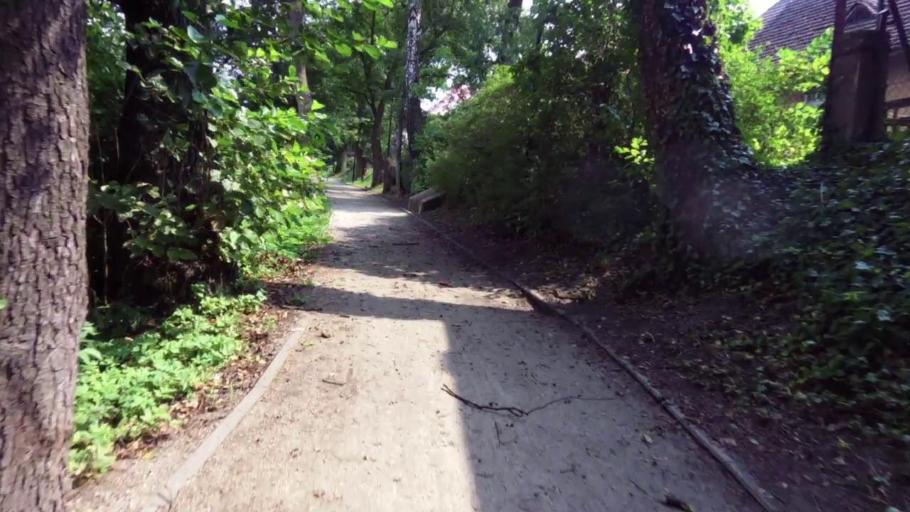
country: PL
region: West Pomeranian Voivodeship
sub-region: Powiat choszczenski
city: Choszczno
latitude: 53.1588
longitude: 15.4133
